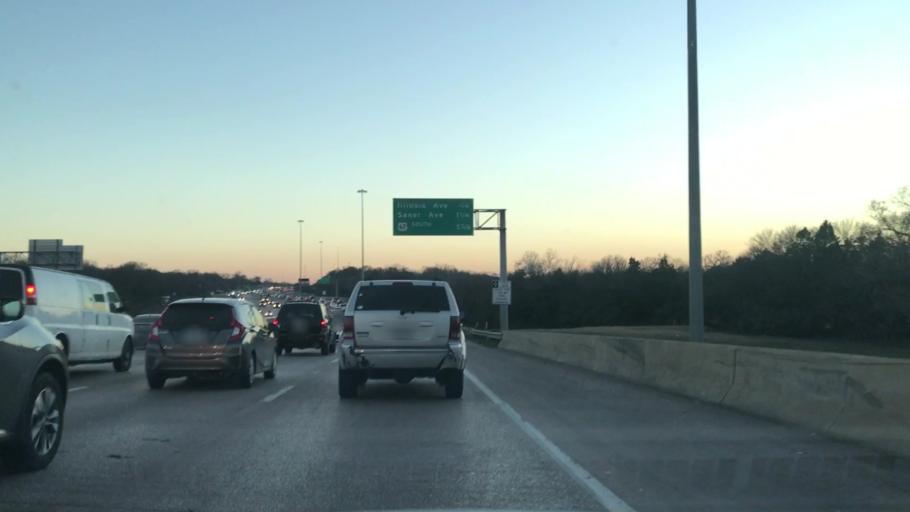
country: US
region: Texas
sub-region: Dallas County
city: Dallas
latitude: 32.7325
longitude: -96.8248
